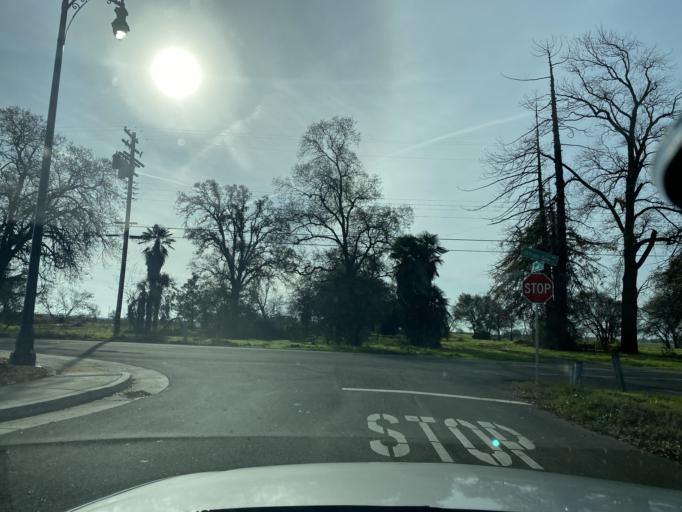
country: US
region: California
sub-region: Sacramento County
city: Elk Grove
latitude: 38.3910
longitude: -121.3878
